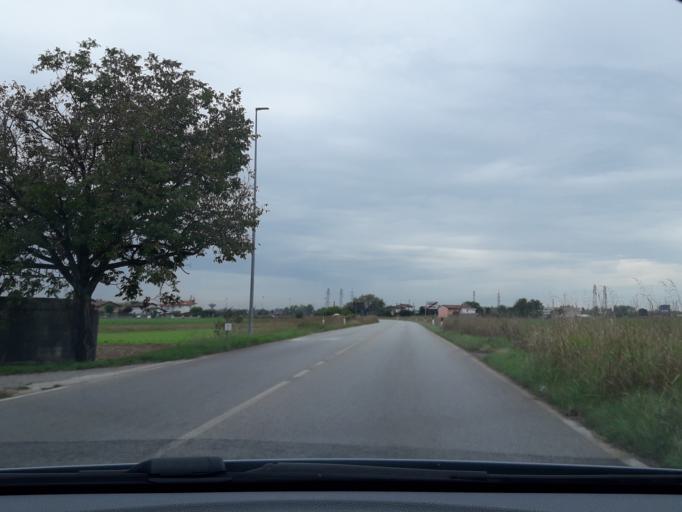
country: IT
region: Friuli Venezia Giulia
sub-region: Provincia di Udine
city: Povoletto
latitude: 46.1033
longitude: 13.2589
